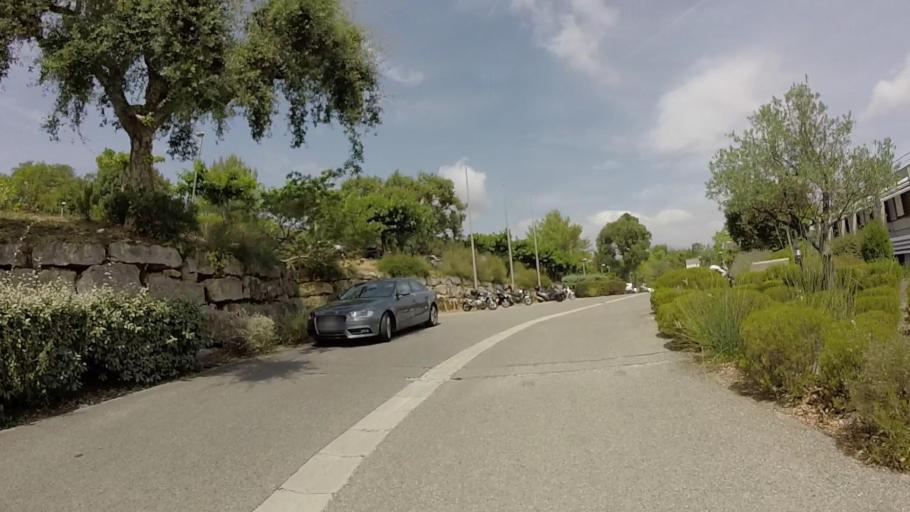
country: FR
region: Provence-Alpes-Cote d'Azur
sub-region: Departement des Alpes-Maritimes
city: Valbonne
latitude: 43.6235
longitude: 7.0295
